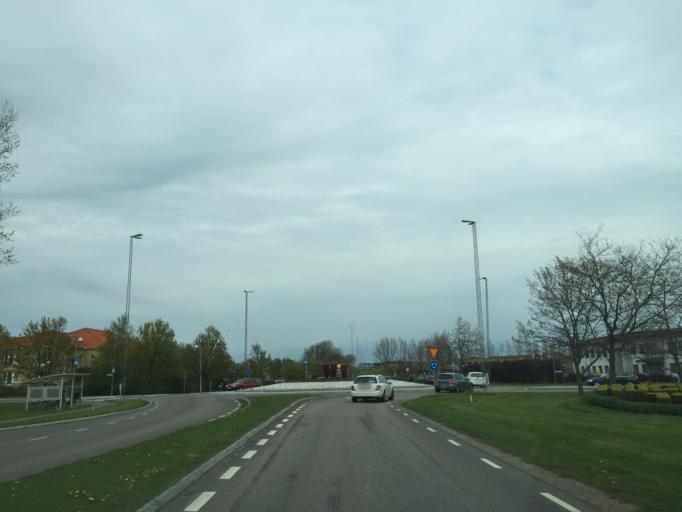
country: SE
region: Skane
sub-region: Hoganas Kommun
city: Hoganas
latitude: 56.1910
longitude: 12.5626
